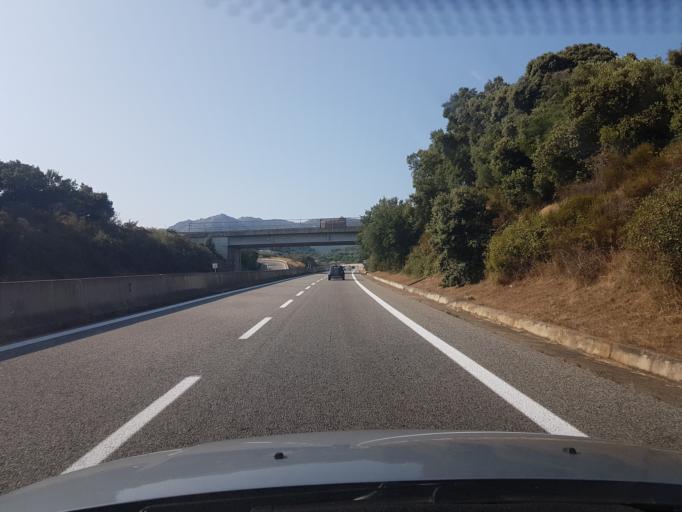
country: IT
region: Sardinia
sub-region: Provincia di Olbia-Tempio
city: Padru
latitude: 40.8066
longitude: 9.5910
